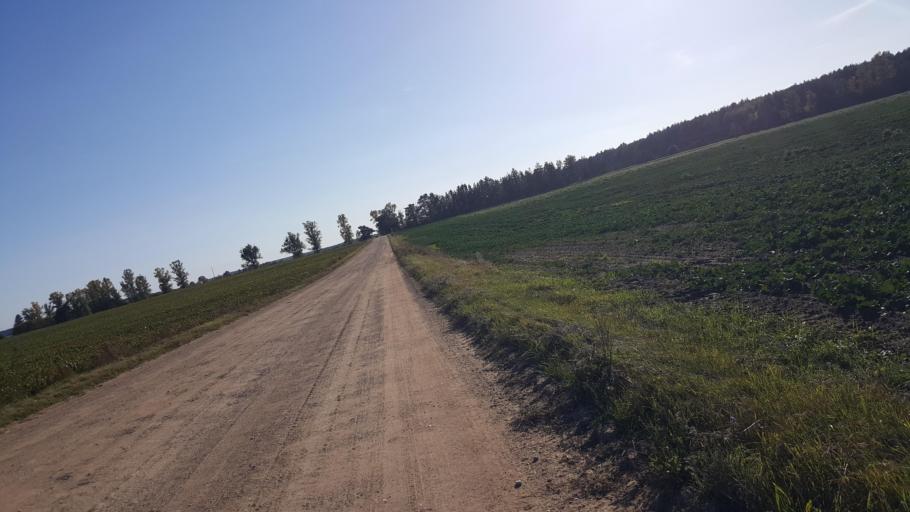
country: BY
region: Brest
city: Kamyanyets
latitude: 52.3786
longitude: 23.8799
